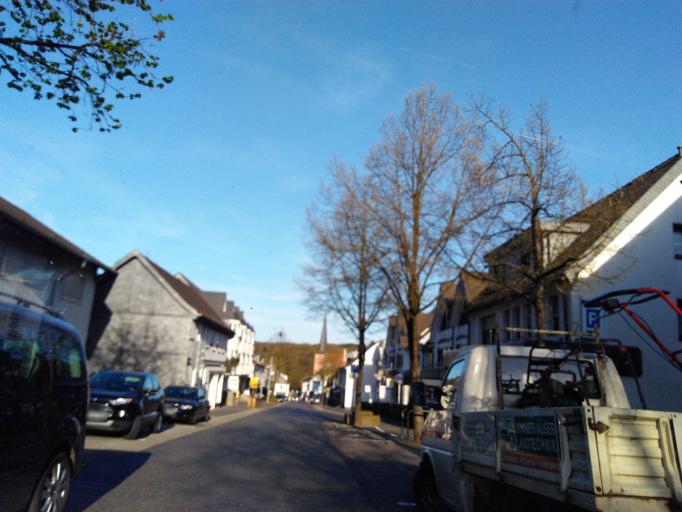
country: DE
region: North Rhine-Westphalia
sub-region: Regierungsbezirk Koln
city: Much
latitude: 50.9055
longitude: 7.4035
